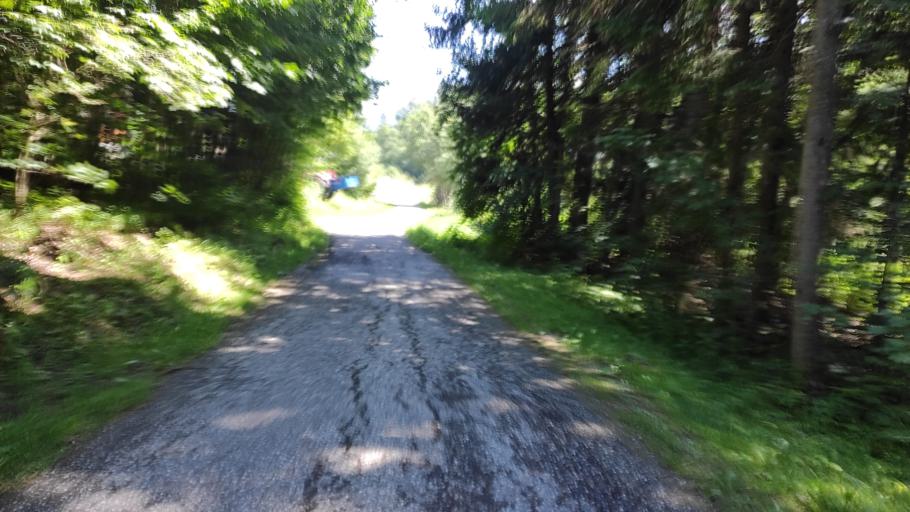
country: AT
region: Salzburg
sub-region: Politischer Bezirk Zell am See
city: Leogang
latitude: 47.4417
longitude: 12.7061
